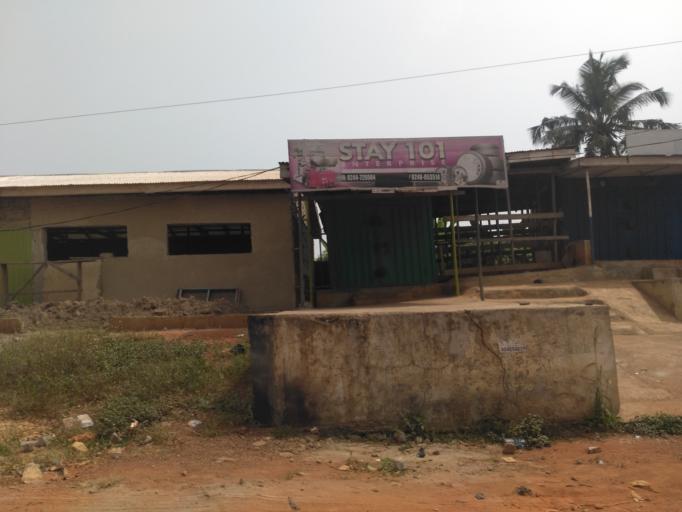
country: GH
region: Ashanti
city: Kumasi
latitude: 6.6422
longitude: -1.6450
